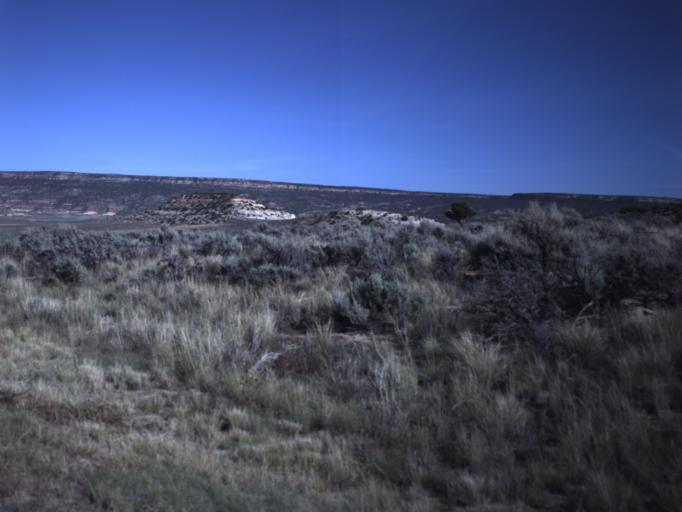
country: US
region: Utah
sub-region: San Juan County
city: Monticello
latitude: 38.0598
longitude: -109.4040
